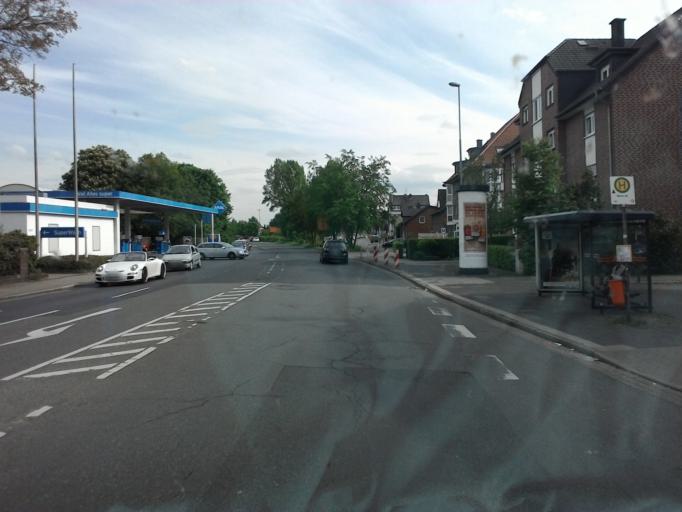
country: DE
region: North Rhine-Westphalia
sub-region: Regierungsbezirk Dusseldorf
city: Moers
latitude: 51.4443
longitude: 6.6603
